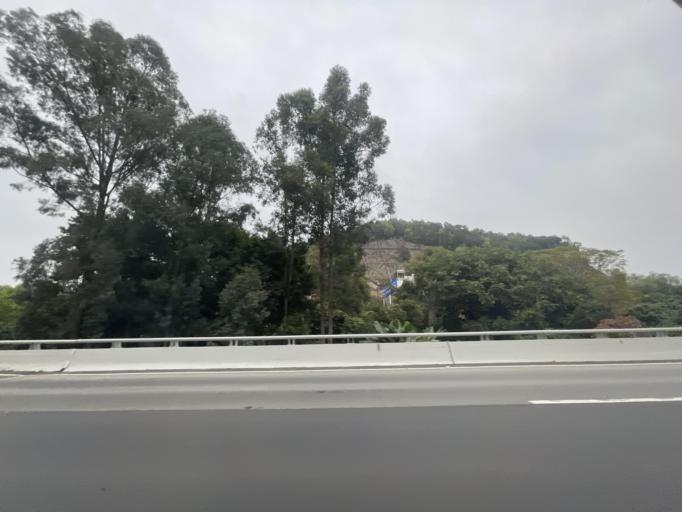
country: CN
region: Guangdong
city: Humen
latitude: 22.8076
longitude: 113.6398
